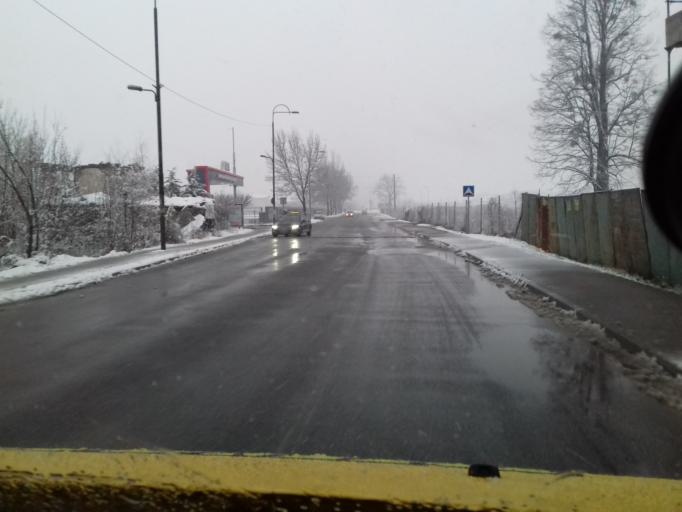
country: BA
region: Federation of Bosnia and Herzegovina
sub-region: Kanton Sarajevo
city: Sarajevo
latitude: 43.8222
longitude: 18.3070
